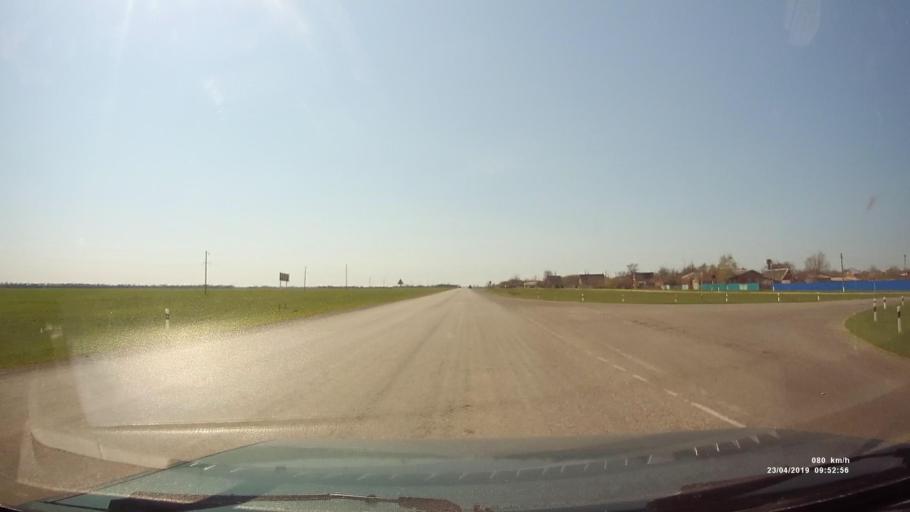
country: RU
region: Rostov
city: Orlovskiy
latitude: 46.8381
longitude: 42.0483
